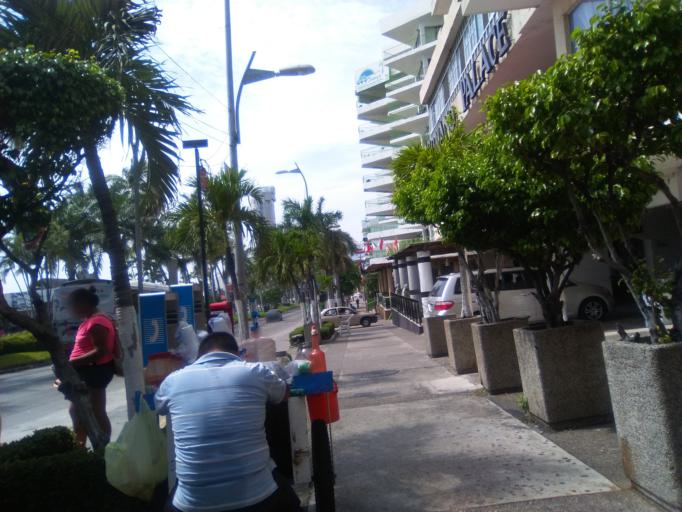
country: MX
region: Guerrero
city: Acapulco de Juarez
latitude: 16.8573
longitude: -99.8678
